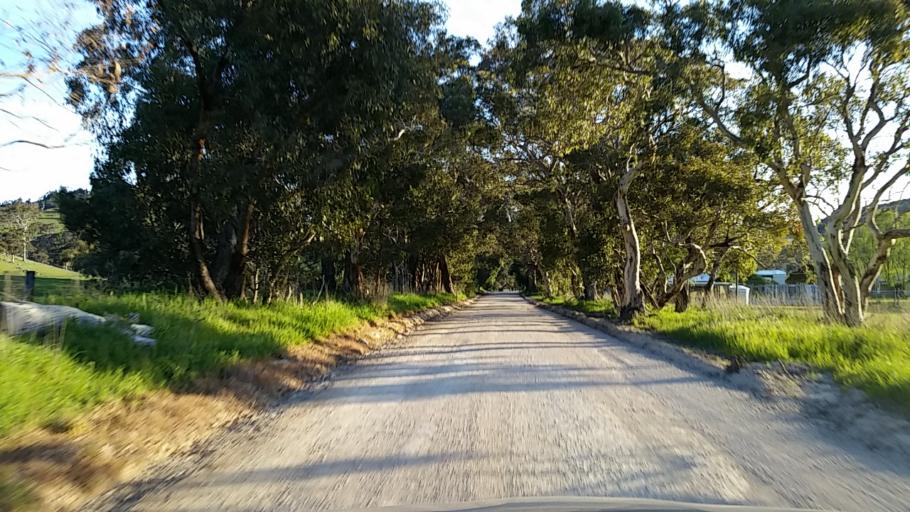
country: AU
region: South Australia
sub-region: Alexandrina
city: Mount Compass
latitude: -35.3184
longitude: 138.6703
